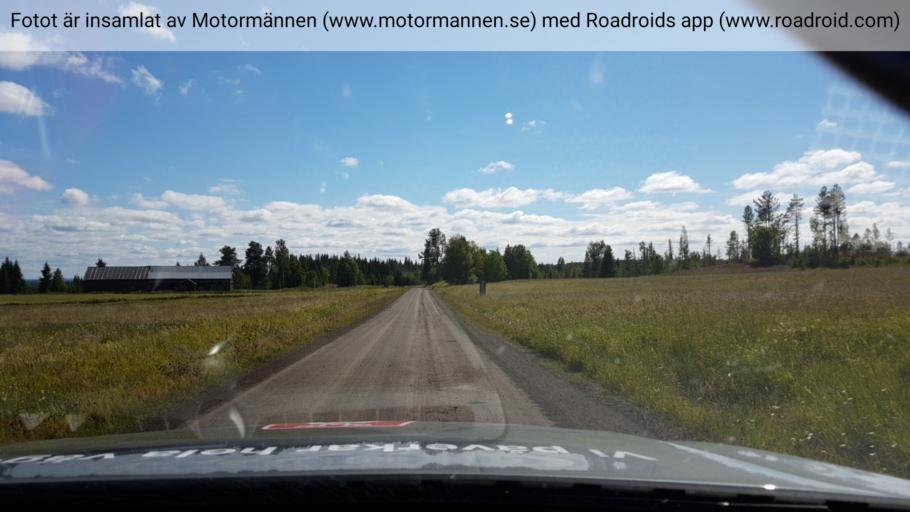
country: SE
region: Jaemtland
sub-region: OEstersunds Kommun
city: Lit
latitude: 63.4412
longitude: 15.2667
